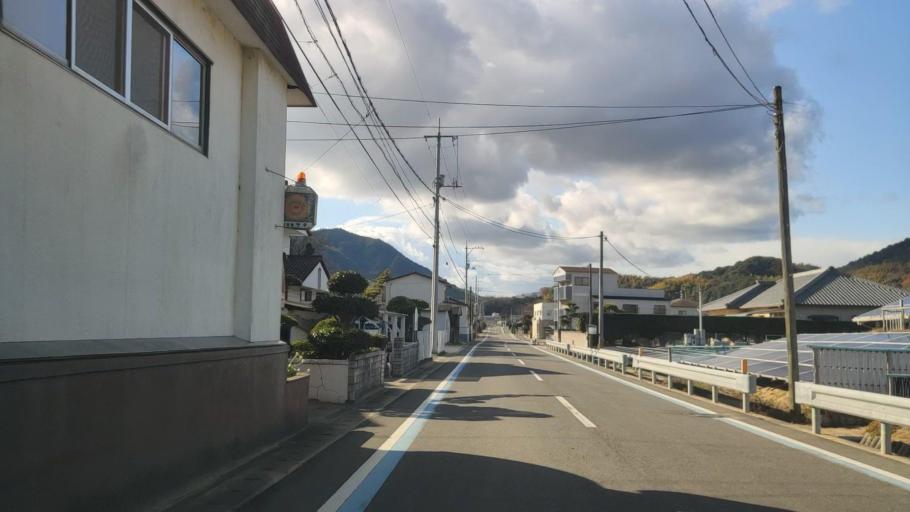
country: JP
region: Hiroshima
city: Innoshima
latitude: 34.2308
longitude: 133.1027
